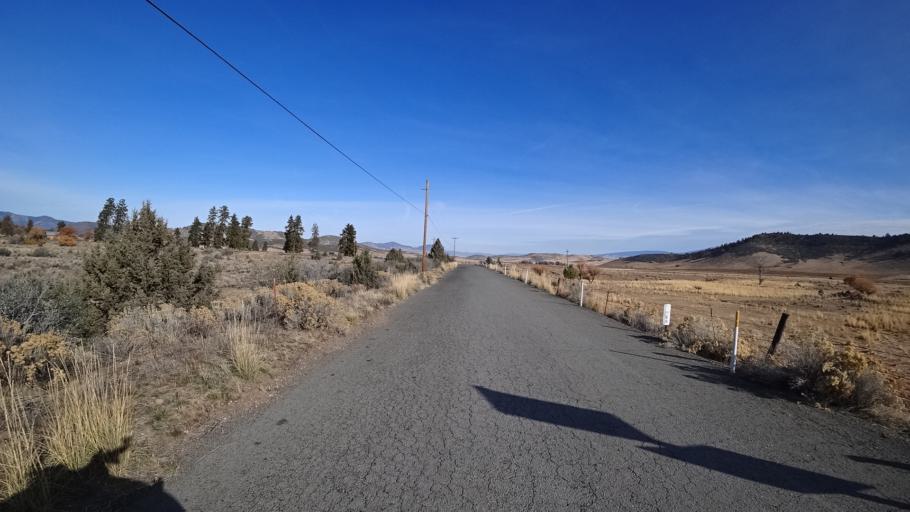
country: US
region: California
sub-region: Siskiyou County
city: Montague
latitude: 41.6350
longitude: -122.5689
